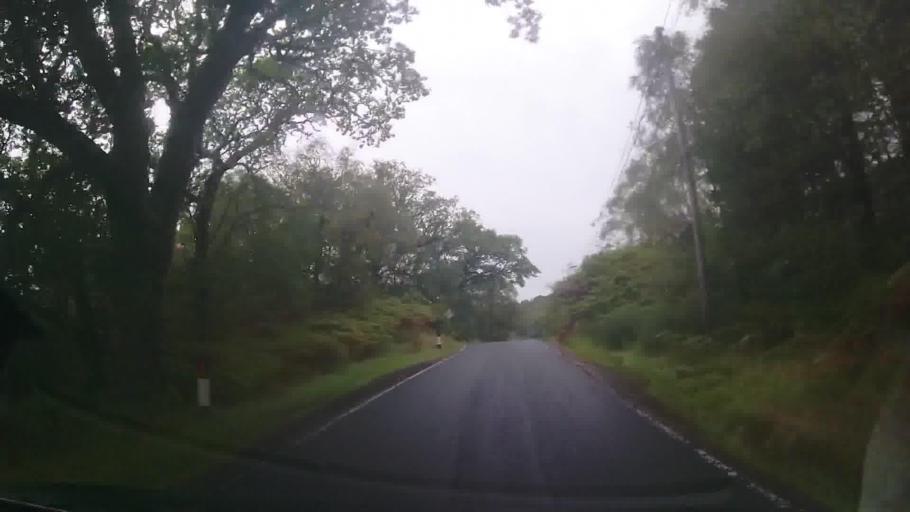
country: GB
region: Scotland
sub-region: Argyll and Bute
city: Isle Of Mull
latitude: 56.7054
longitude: -5.7115
